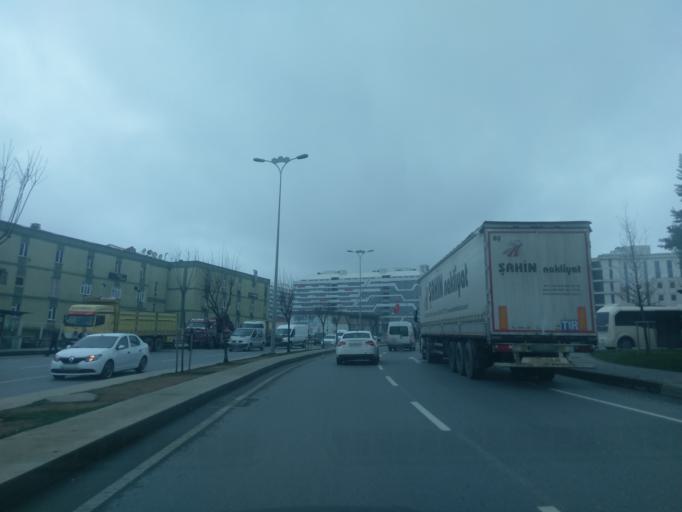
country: TR
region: Istanbul
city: Basaksehir
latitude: 41.0788
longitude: 28.7935
